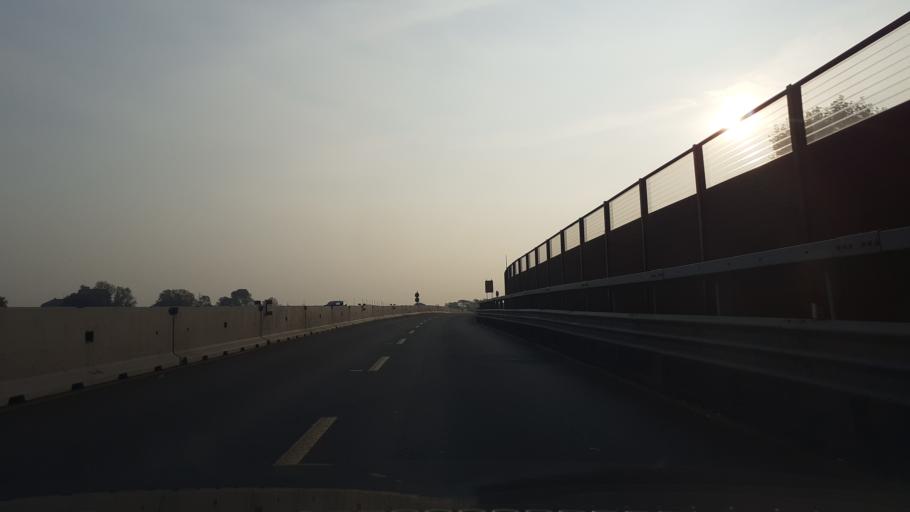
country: IT
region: Lombardy
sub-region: Citta metropolitana di Milano
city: Paderno Dugnano
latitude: 45.5580
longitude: 9.1611
